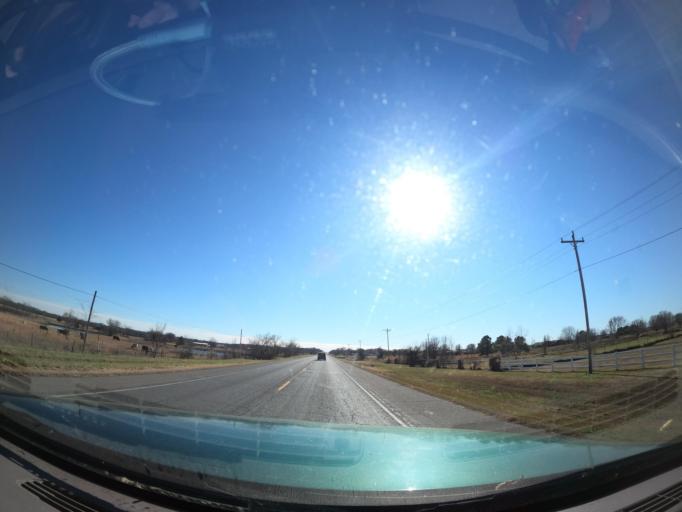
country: US
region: Oklahoma
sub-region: Muskogee County
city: Haskell
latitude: 35.8550
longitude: -95.6775
